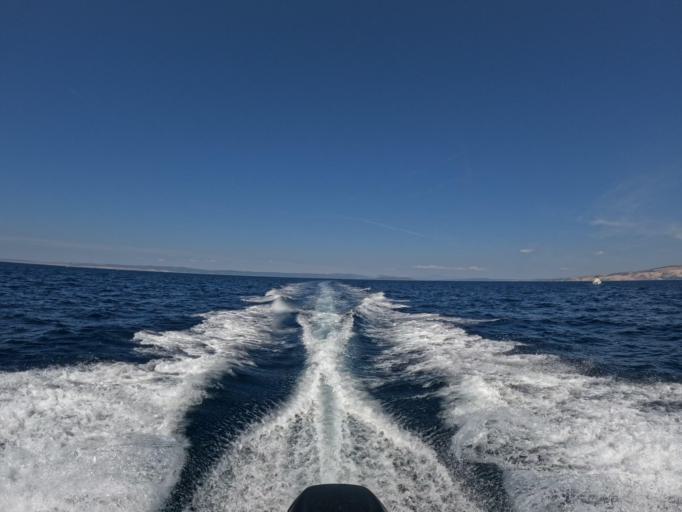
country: HR
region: Primorsko-Goranska
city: Lopar
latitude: 44.8727
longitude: 14.6675
